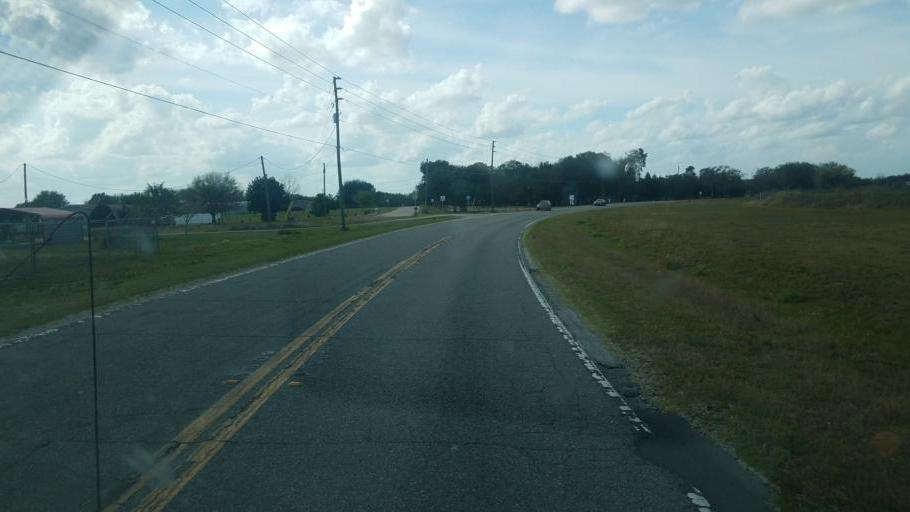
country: US
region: Florida
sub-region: Polk County
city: Haines City
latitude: 28.0773
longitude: -81.5791
